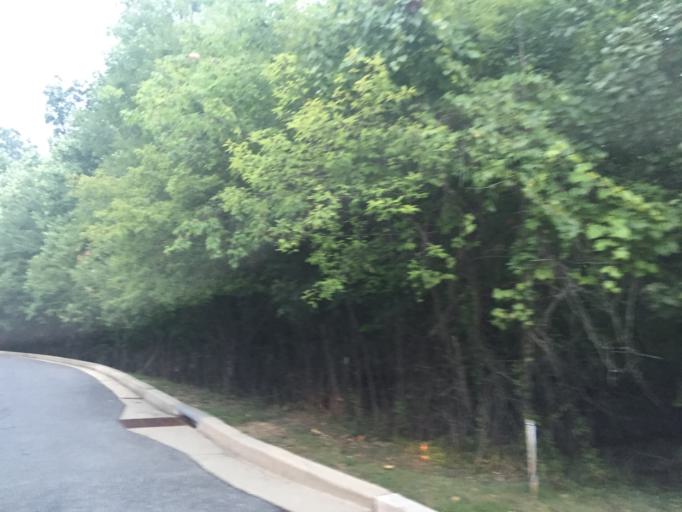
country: US
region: Maryland
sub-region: Baltimore County
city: Perry Hall
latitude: 39.4084
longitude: -76.4912
